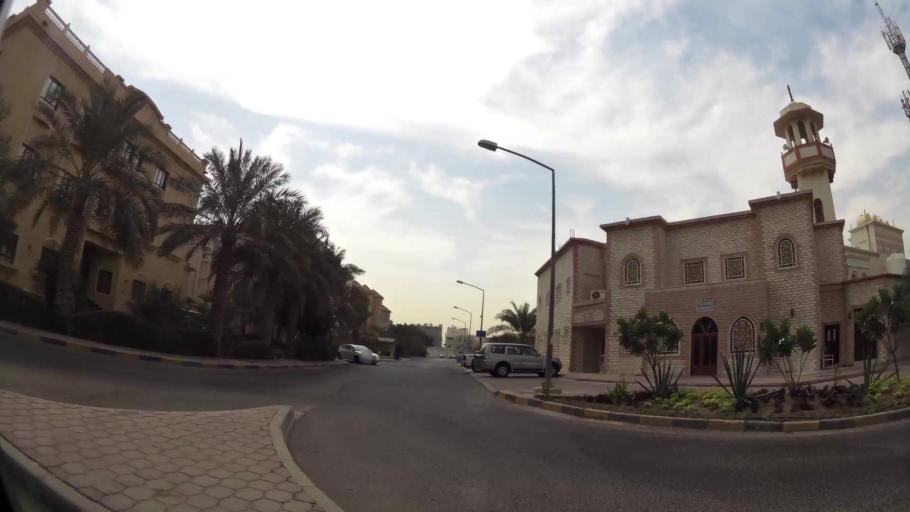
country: KW
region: Mubarak al Kabir
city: Sabah as Salim
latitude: 29.2711
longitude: 48.0282
